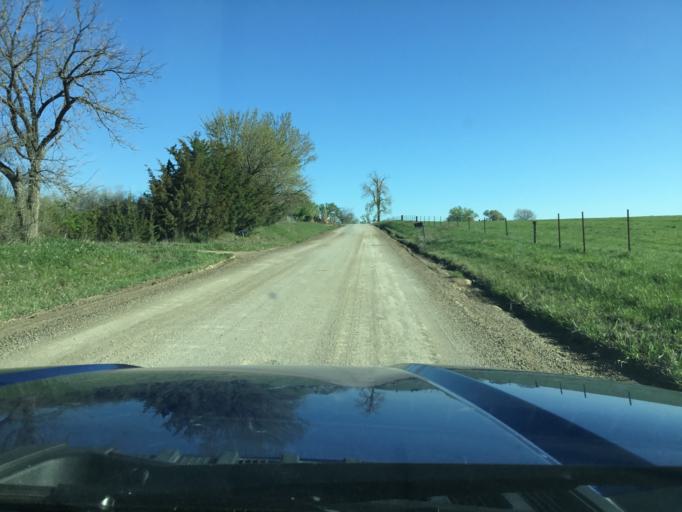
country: US
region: Kansas
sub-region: Douglas County
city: Lawrence
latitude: 38.9653
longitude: -95.3724
